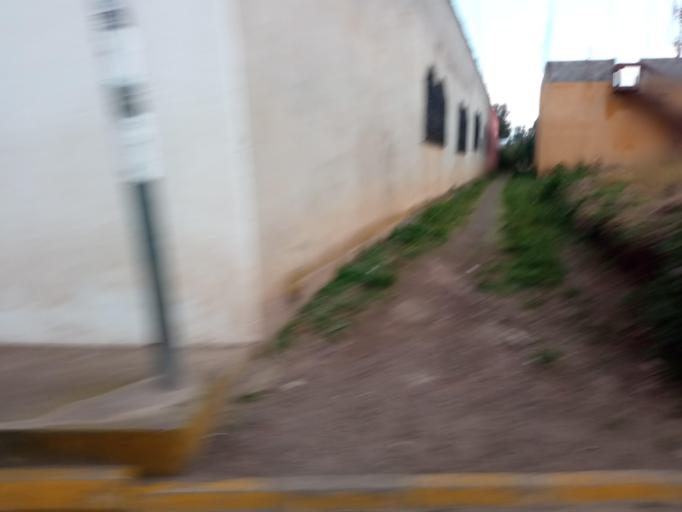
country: GT
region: Quetzaltenango
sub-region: Municipio de La Esperanza
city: La Esperanza
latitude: 14.8550
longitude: -91.5516
